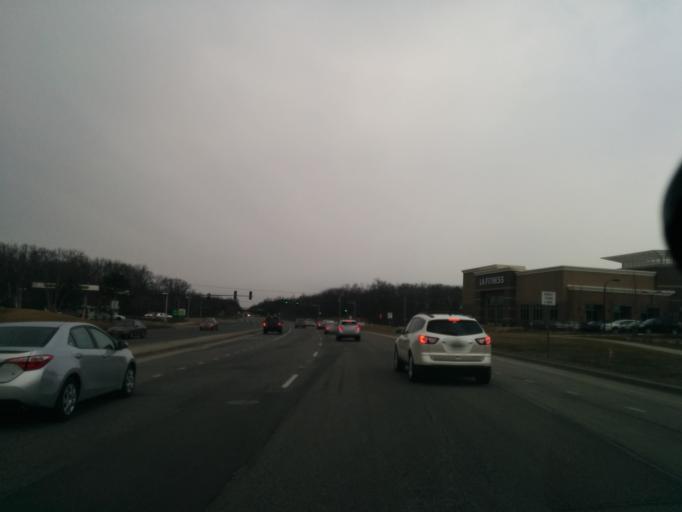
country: US
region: Illinois
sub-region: Cook County
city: Northbrook
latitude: 42.1092
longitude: -87.8744
